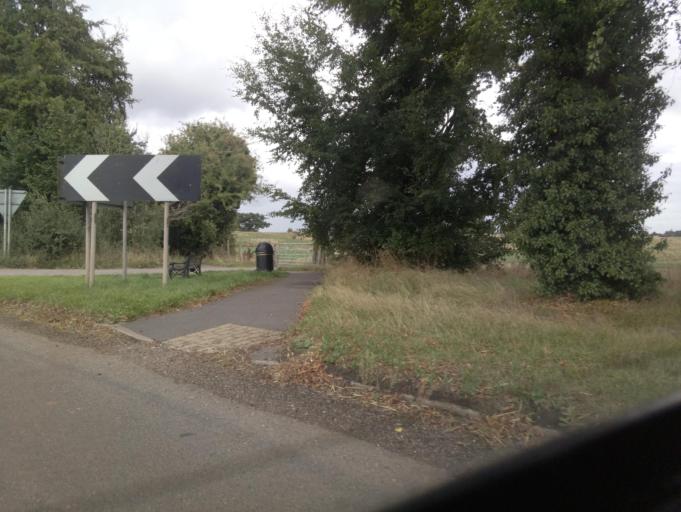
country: GB
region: England
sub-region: Staffordshire
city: Eccleshall
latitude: 52.8642
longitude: -2.2524
